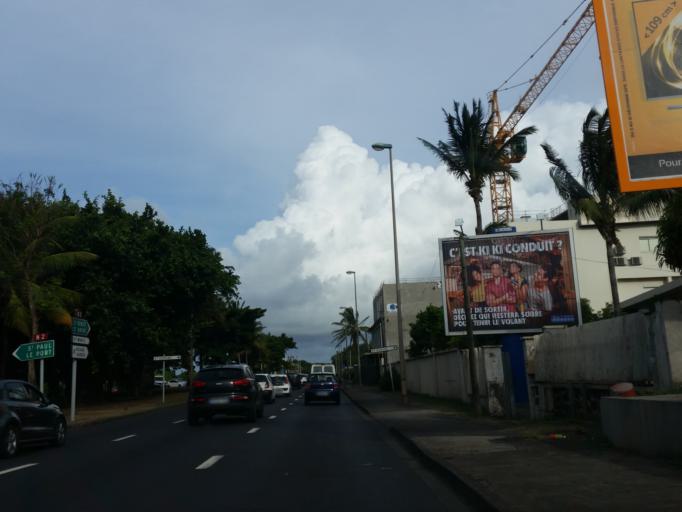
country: RE
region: Reunion
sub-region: Reunion
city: Saint-Denis
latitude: -20.8863
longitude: 55.4811
